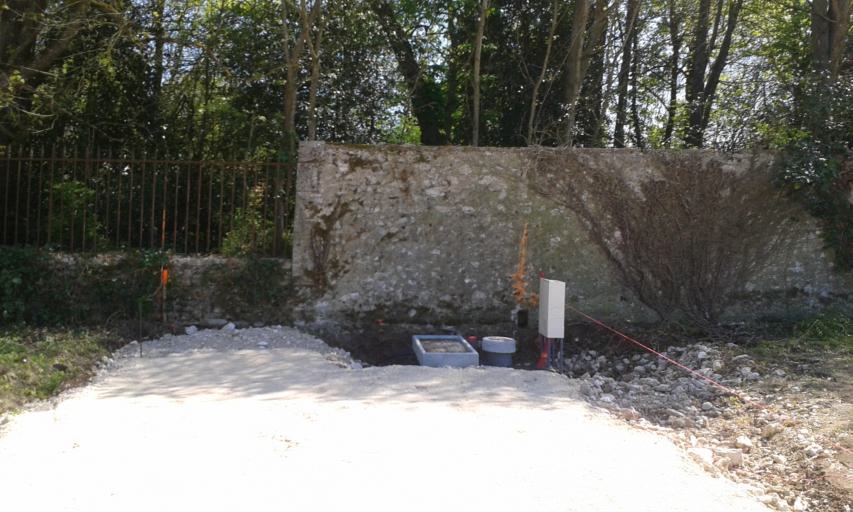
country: FR
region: Centre
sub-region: Departement du Loiret
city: Beaugency
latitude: 47.7788
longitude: 1.6233
